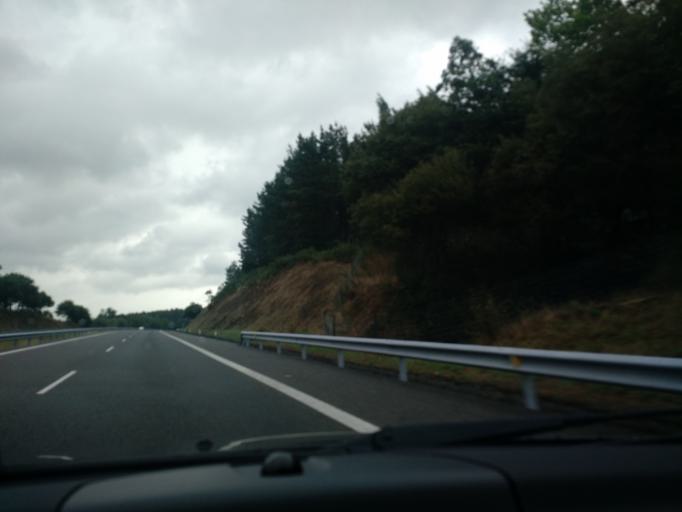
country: ES
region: Galicia
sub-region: Provincia da Coruna
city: Ordes
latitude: 43.0278
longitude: -8.4012
